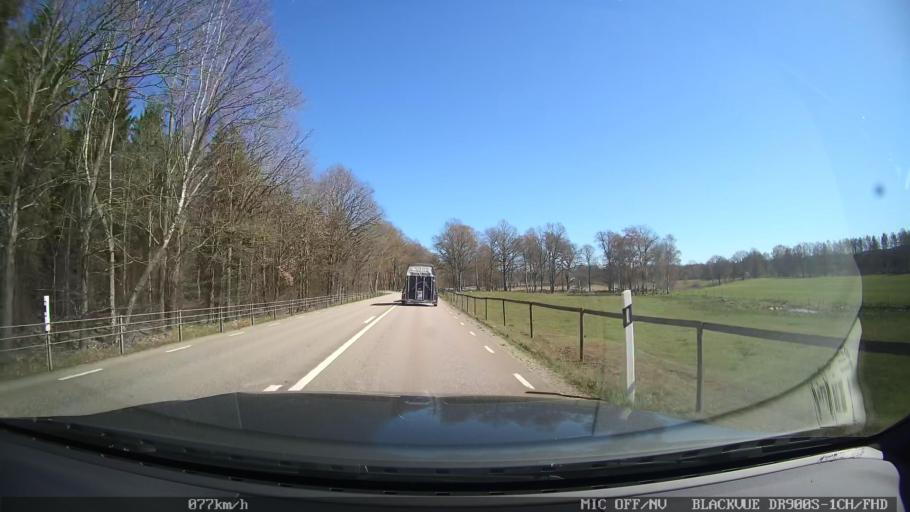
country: SE
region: Skane
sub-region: Klippans Kommun
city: Ljungbyhed
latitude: 56.0961
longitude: 13.1982
